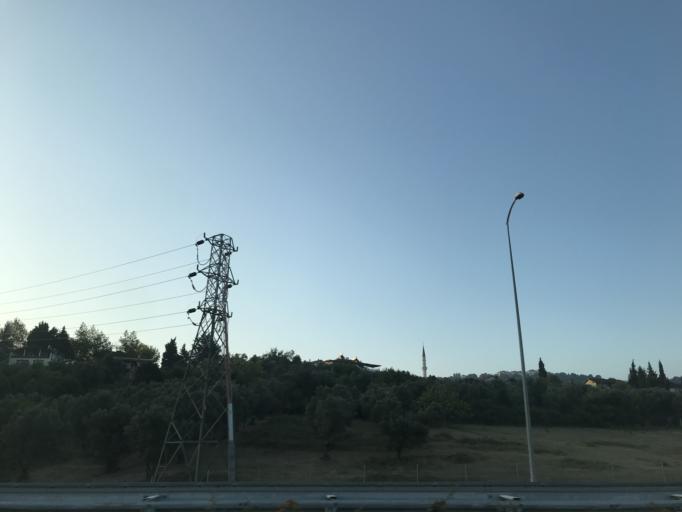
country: TR
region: Yalova
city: Altinova
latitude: 40.6888
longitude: 29.4743
